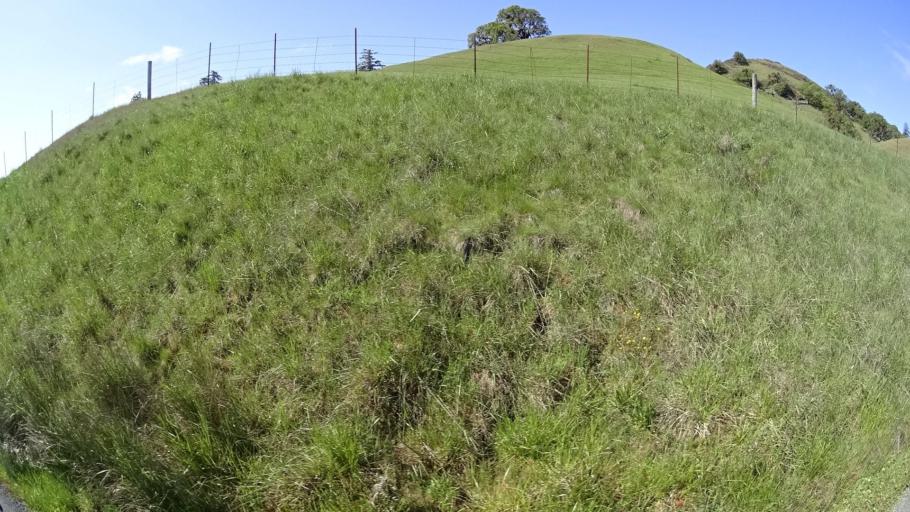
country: US
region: California
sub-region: Humboldt County
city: Redway
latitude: 40.0806
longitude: -123.6544
